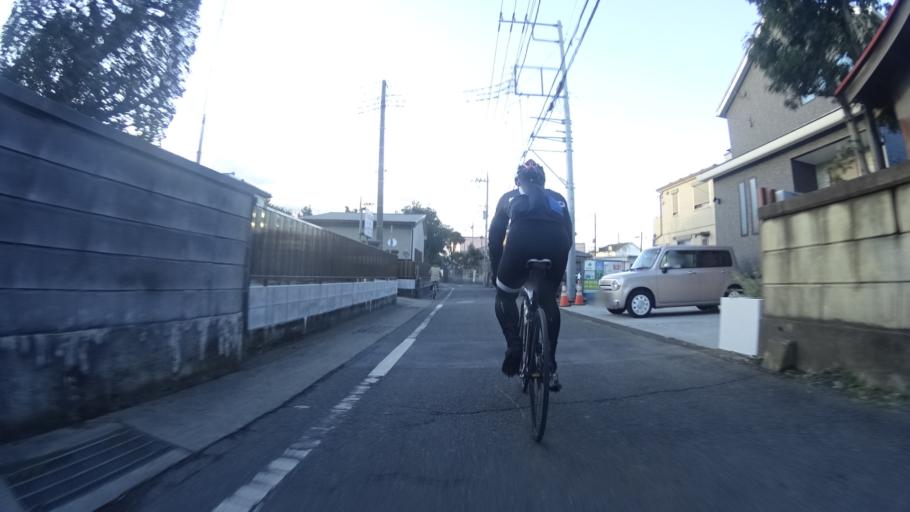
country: JP
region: Kanagawa
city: Atsugi
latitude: 35.4607
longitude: 139.3681
